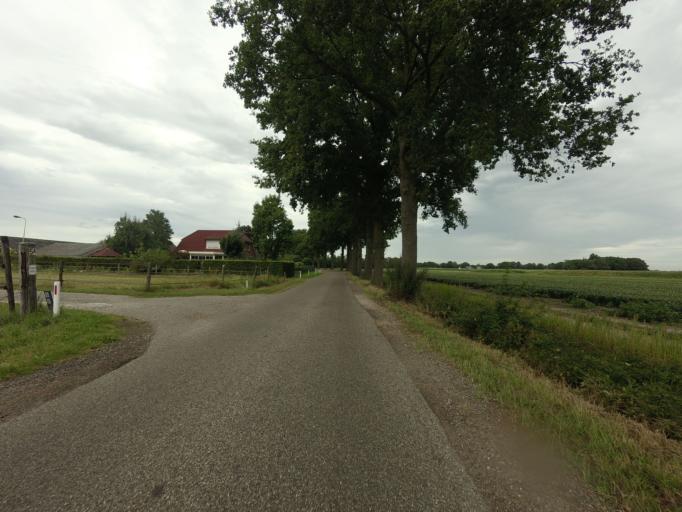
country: NL
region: Overijssel
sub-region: Gemeente Raalte
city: Raalte
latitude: 52.3593
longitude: 6.3563
